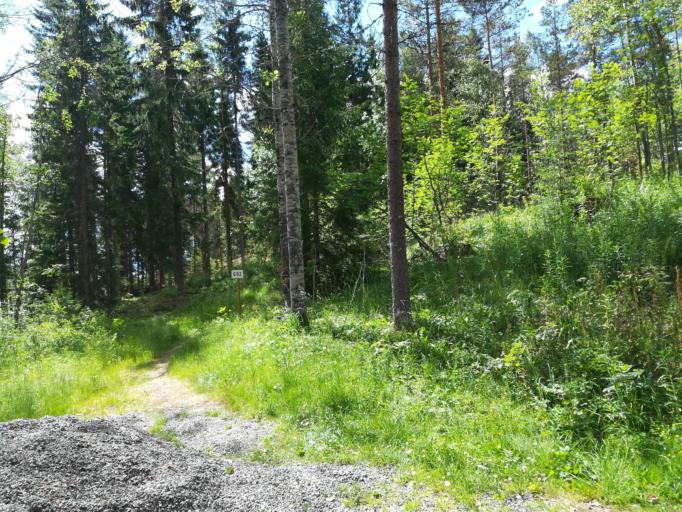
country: FI
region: Southern Savonia
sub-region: Mikkeli
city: Maentyharju
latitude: 61.3663
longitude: 26.9331
